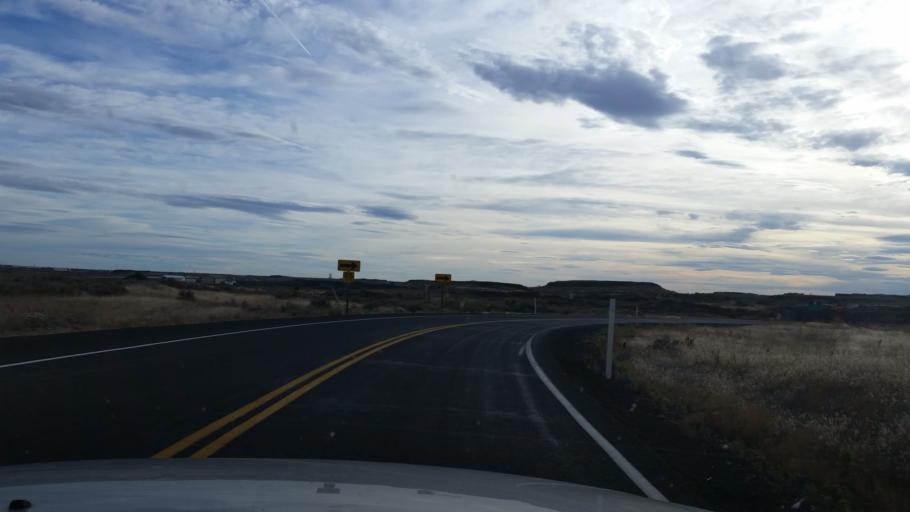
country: US
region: Washington
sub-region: Lincoln County
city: Davenport
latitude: 47.3168
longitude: -117.9731
